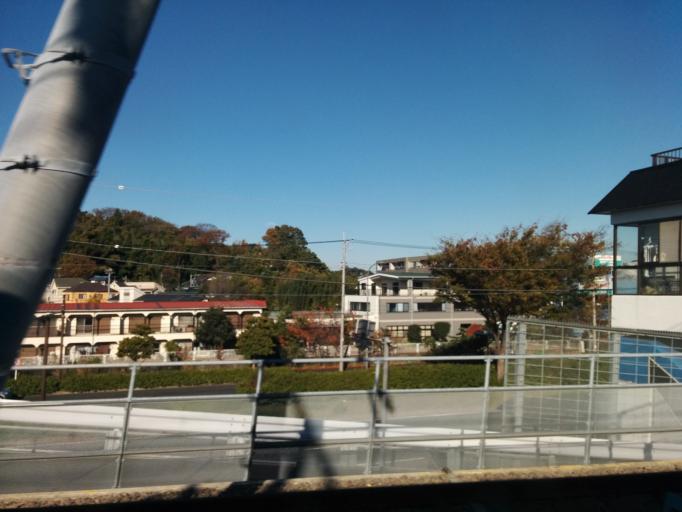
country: JP
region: Kanagawa
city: Yokohama
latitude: 35.4985
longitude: 139.6066
